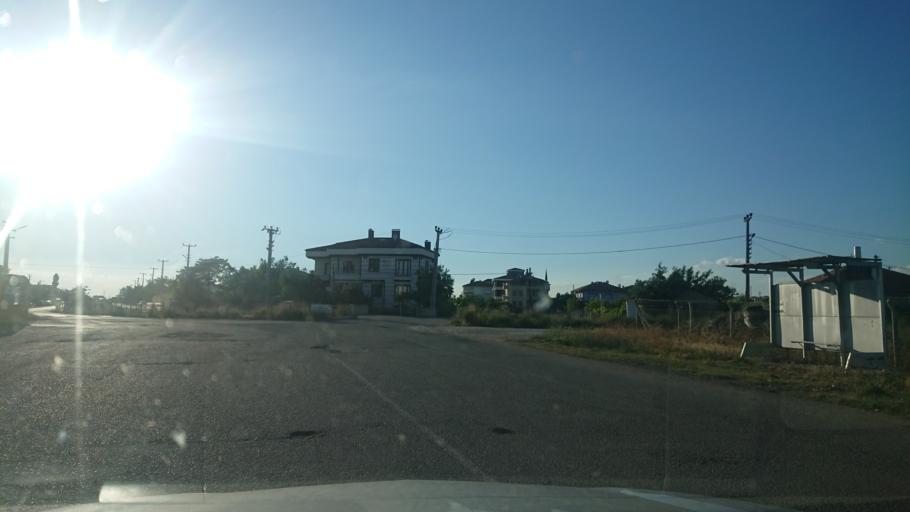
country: TR
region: Aksaray
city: Aksaray
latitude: 38.3897
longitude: 33.9973
